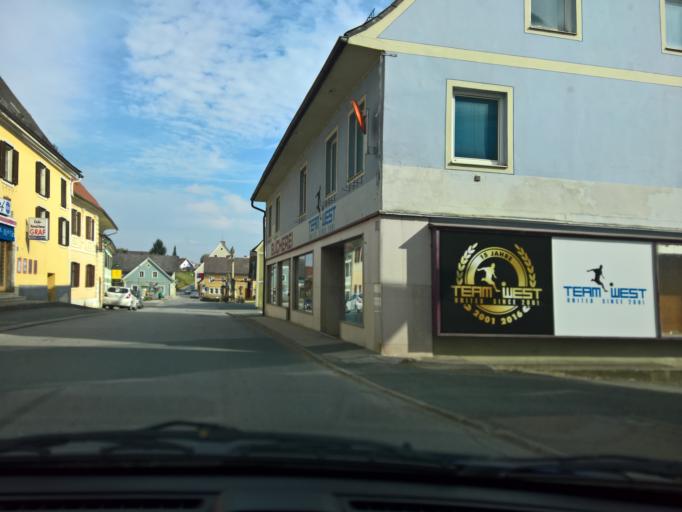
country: AT
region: Styria
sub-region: Politischer Bezirk Deutschlandsberg
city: Gross Sankt Florian
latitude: 46.8241
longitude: 15.3172
